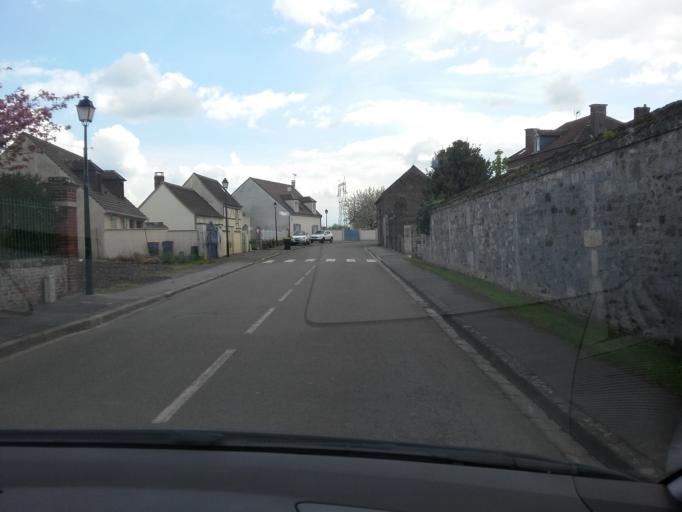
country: FR
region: Picardie
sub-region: Departement de l'Oise
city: Longueil-Sainte-Marie
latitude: 49.3719
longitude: 2.6991
